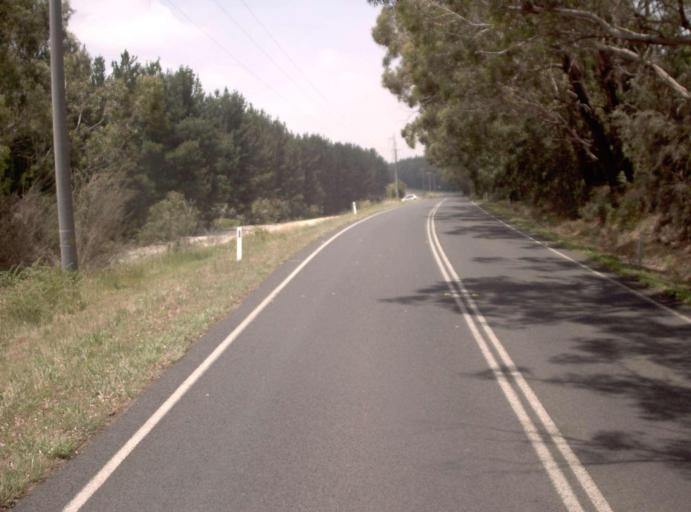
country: AU
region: Victoria
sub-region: Latrobe
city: Traralgon
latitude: -38.2572
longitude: 146.6775
